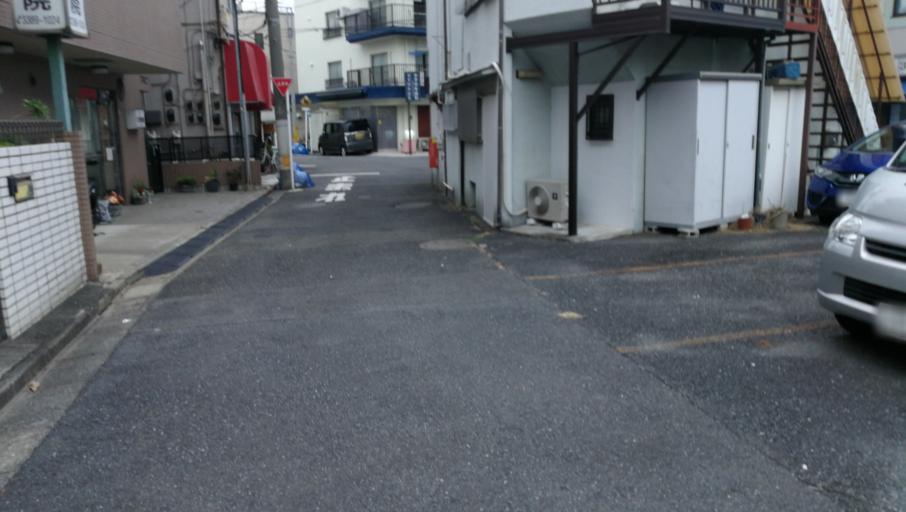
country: JP
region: Tokyo
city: Tokyo
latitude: 35.7256
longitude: 139.6682
